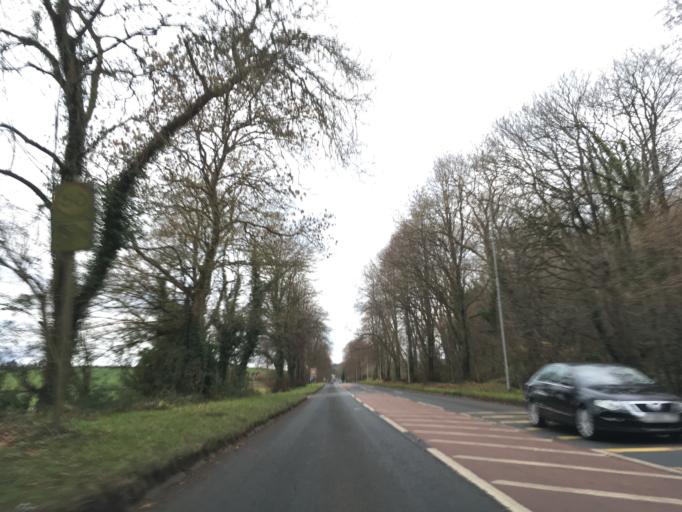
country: GB
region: Wales
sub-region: Newport
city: Llanvaches
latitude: 51.6148
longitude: -2.8337
